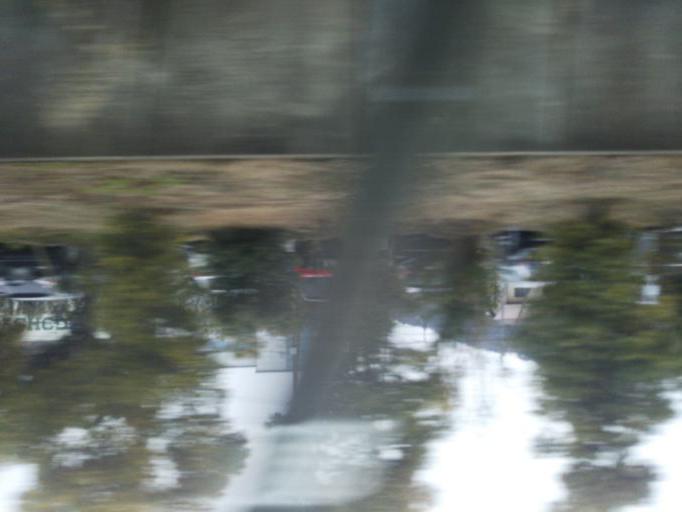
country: JP
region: Shiga Prefecture
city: Moriyama
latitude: 35.0213
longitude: 136.0469
